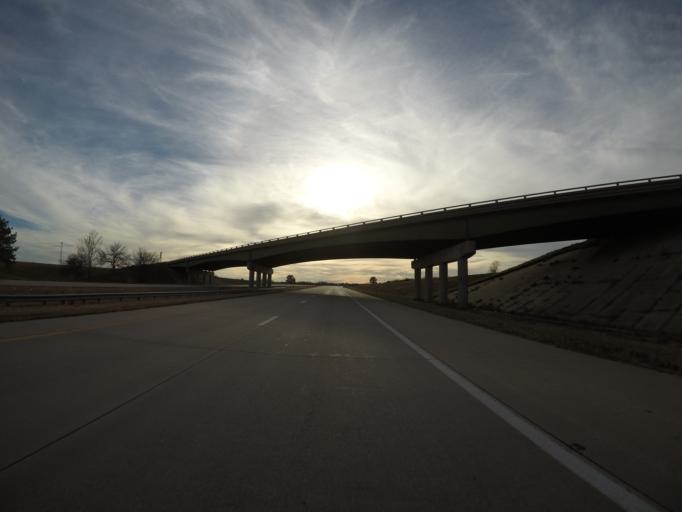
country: US
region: Kansas
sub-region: Franklin County
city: Ottawa
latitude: 38.5359
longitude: -95.3783
